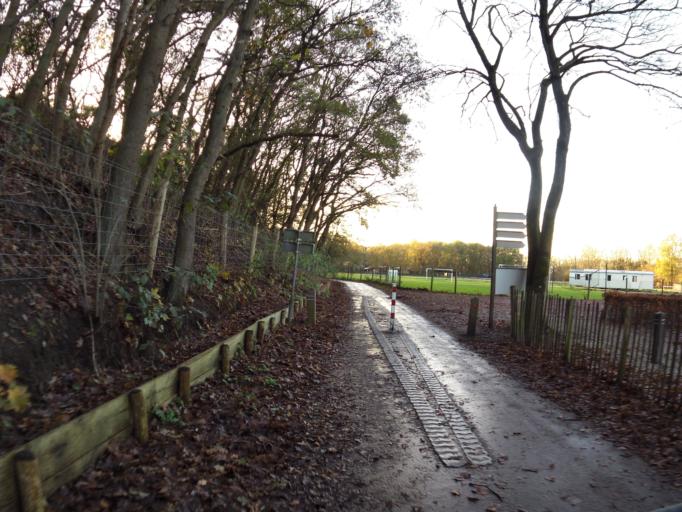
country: NL
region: North Brabant
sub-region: Gemeente Waalwijk
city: Waalwijk
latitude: 51.6570
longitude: 5.0878
